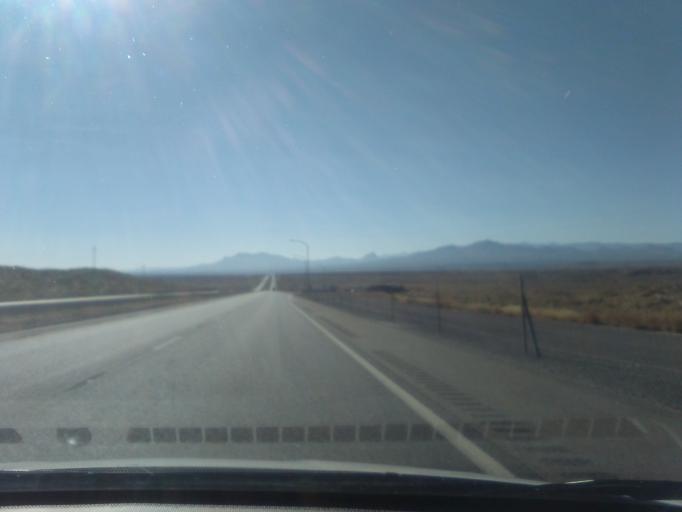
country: US
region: New Mexico
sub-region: Socorro County
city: Socorro
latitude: 34.3092
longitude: -106.8885
